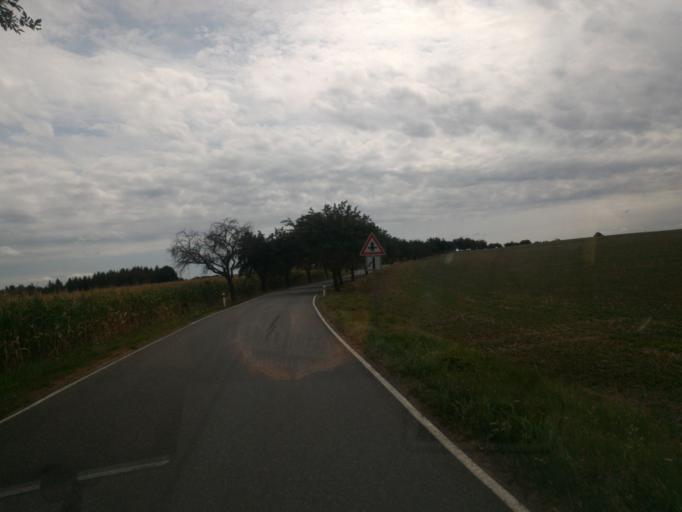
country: CZ
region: Jihocesky
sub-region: Okres Jindrichuv Hradec
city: Dacice
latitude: 49.0954
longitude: 15.4215
